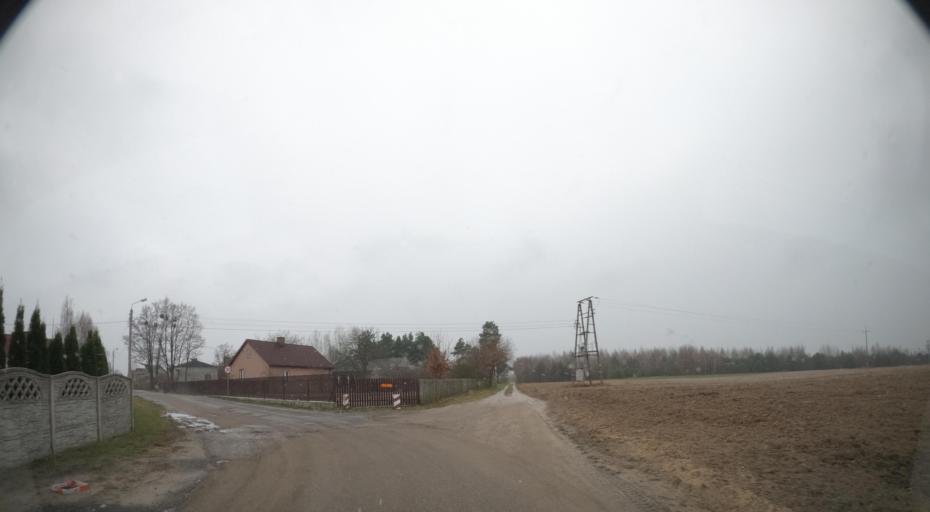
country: PL
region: Masovian Voivodeship
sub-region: Powiat radomski
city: Jedlnia-Letnisko
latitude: 51.3994
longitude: 21.2743
